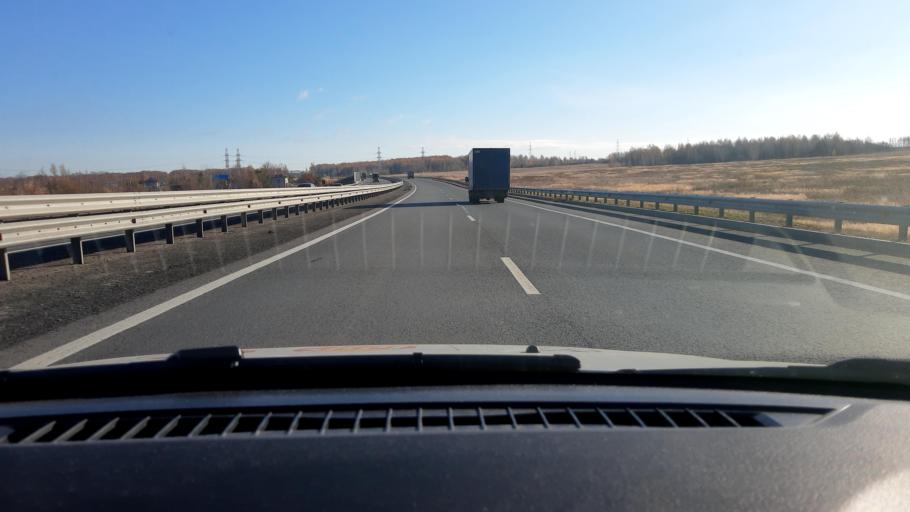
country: RU
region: Nizjnij Novgorod
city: Burevestnik
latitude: 56.1141
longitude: 43.8639
